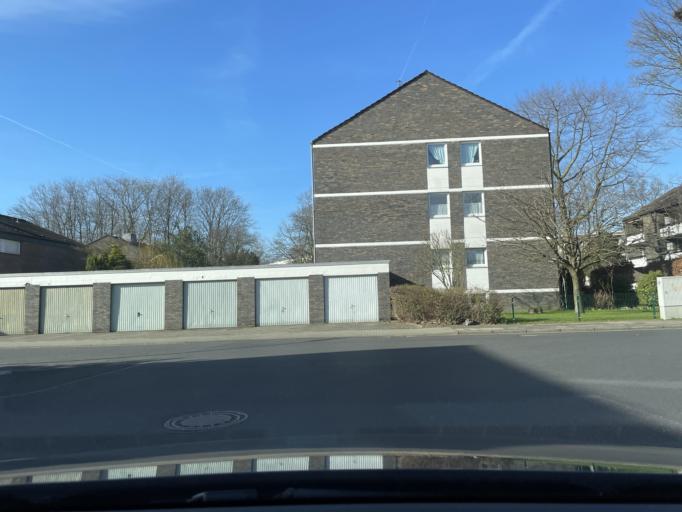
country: DE
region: North Rhine-Westphalia
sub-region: Regierungsbezirk Dusseldorf
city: Neuss
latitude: 51.2121
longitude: 6.6607
